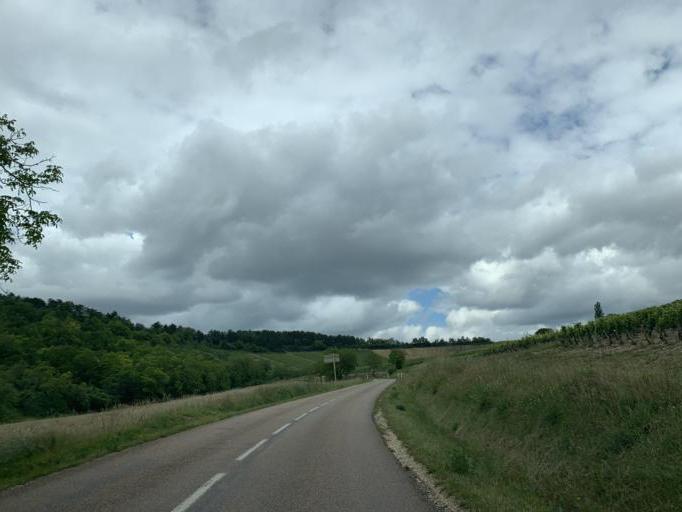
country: FR
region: Bourgogne
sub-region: Departement de l'Yonne
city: Saint-Bris-le-Vineux
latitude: 47.7152
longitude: 3.6720
